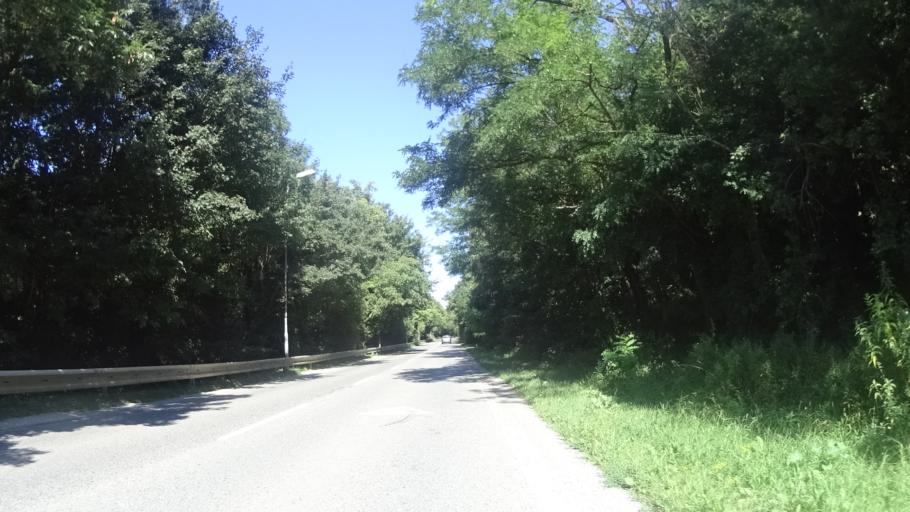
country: AT
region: Lower Austria
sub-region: Politischer Bezirk Bruck an der Leitha
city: Wolfsthal
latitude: 48.1663
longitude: 16.9960
